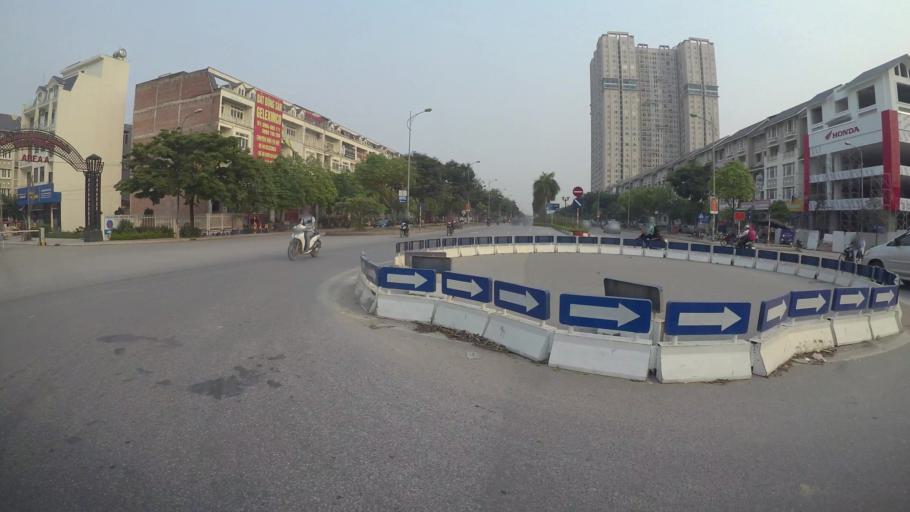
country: VN
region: Ha Noi
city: Cau Dien
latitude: 21.0057
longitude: 105.7320
